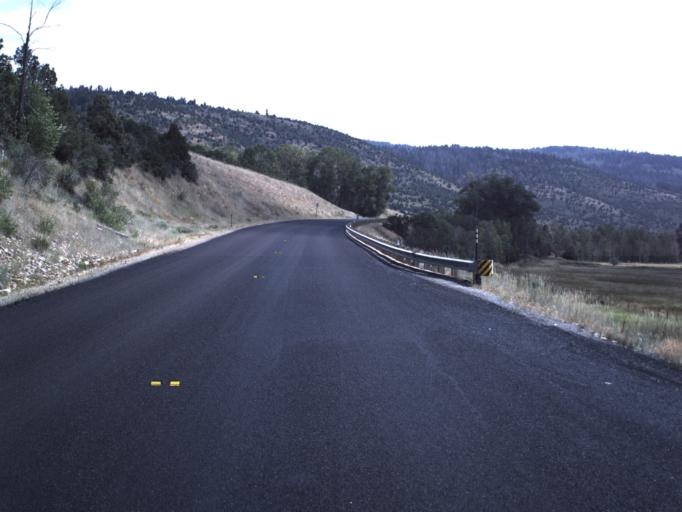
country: US
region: Utah
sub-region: Summit County
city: Francis
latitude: 40.5582
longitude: -111.1316
